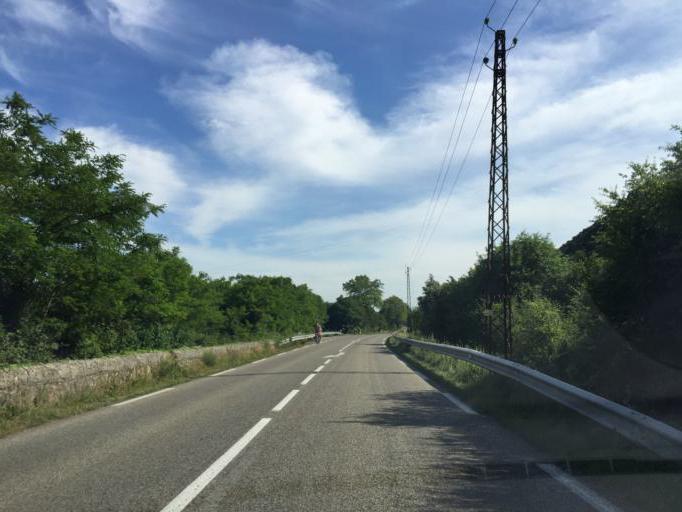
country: FR
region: Rhone-Alpes
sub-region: Departement de l'Ardeche
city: Cruas
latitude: 44.6789
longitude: 4.7714
